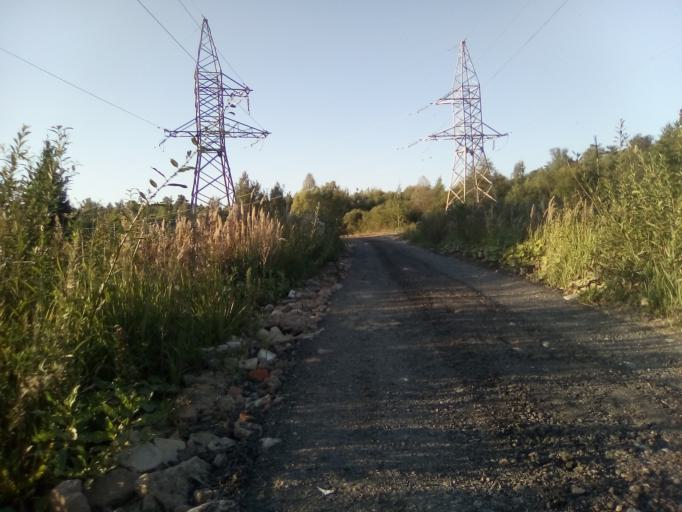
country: RU
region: Moskovskaya
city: Aprelevka
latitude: 55.5788
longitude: 37.0656
